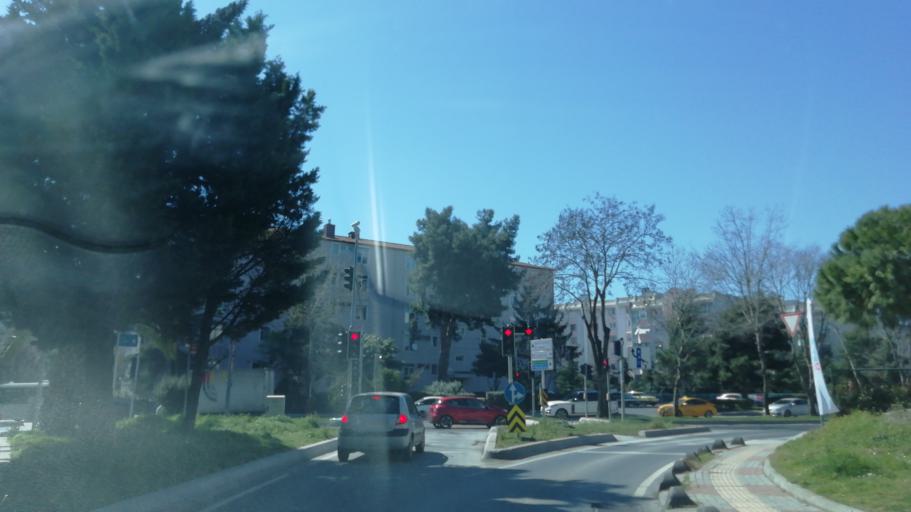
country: TR
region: Istanbul
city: Bahcelievler
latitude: 40.9861
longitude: 28.8566
